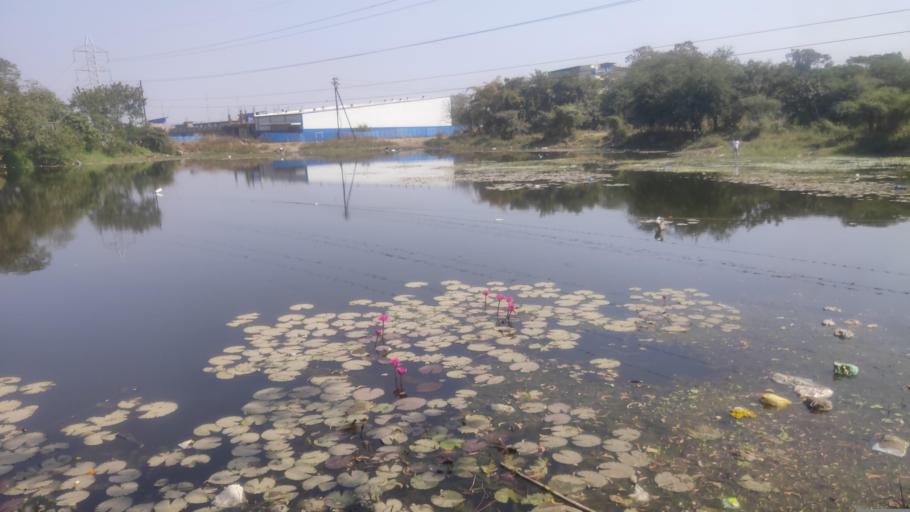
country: IN
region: Maharashtra
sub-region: Thane
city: Bhiwandi
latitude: 19.2593
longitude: 73.0698
